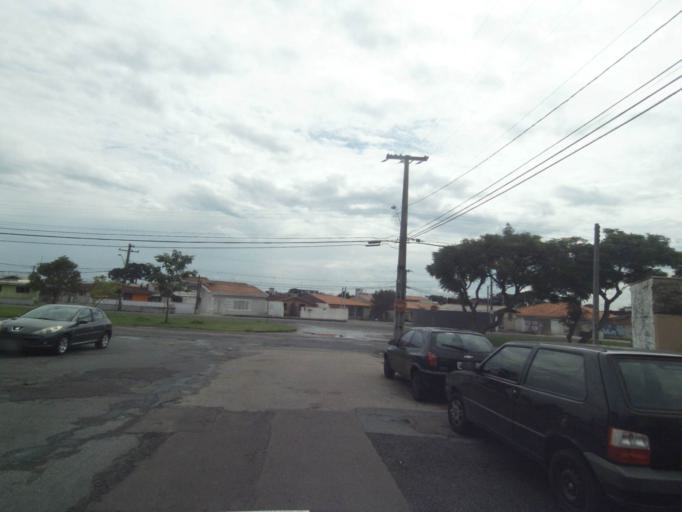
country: BR
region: Parana
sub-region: Pinhais
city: Pinhais
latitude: -25.4718
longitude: -49.2017
